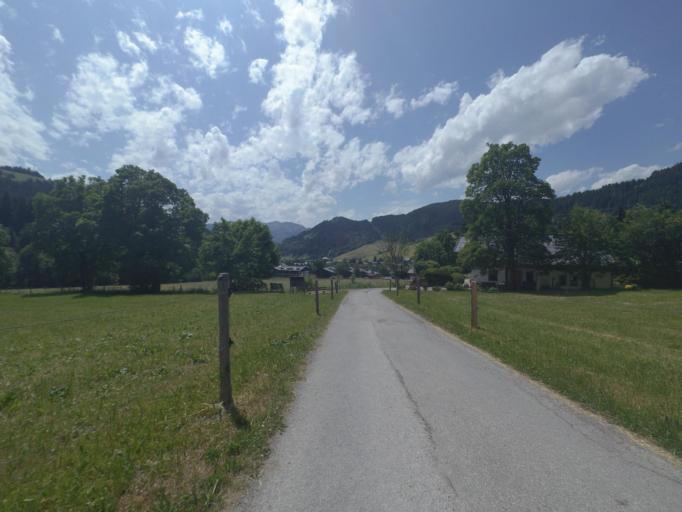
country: AT
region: Salzburg
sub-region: Politischer Bezirk Zell am See
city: Dienten am Hochkonig
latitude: 47.4106
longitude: 12.9839
